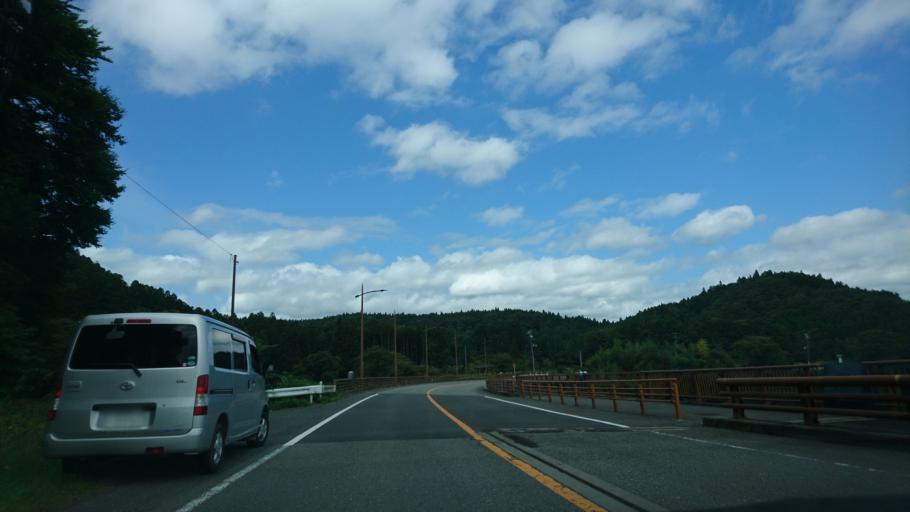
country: JP
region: Miyagi
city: Furukawa
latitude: 38.7779
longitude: 140.8527
